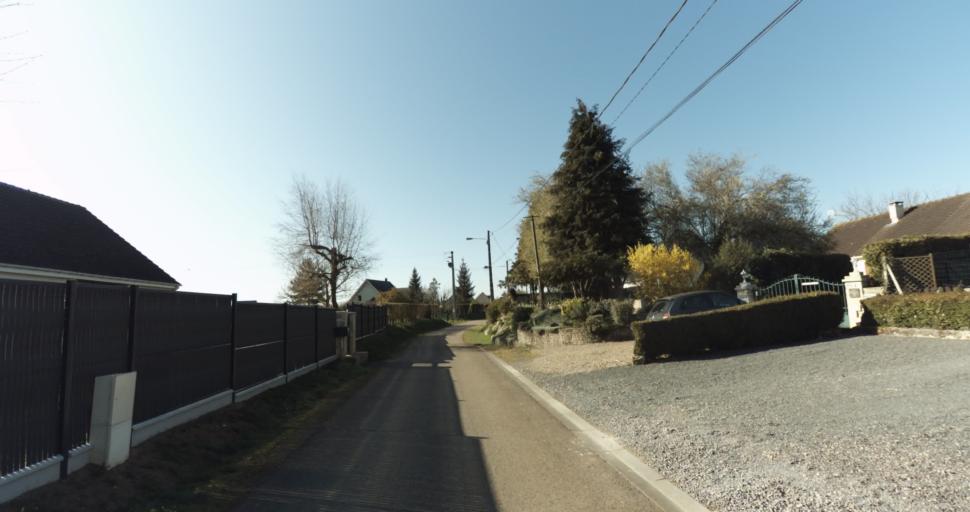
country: FR
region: Lower Normandy
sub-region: Departement du Calvados
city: Saint-Pierre-sur-Dives
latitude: 48.9921
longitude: -0.0168
